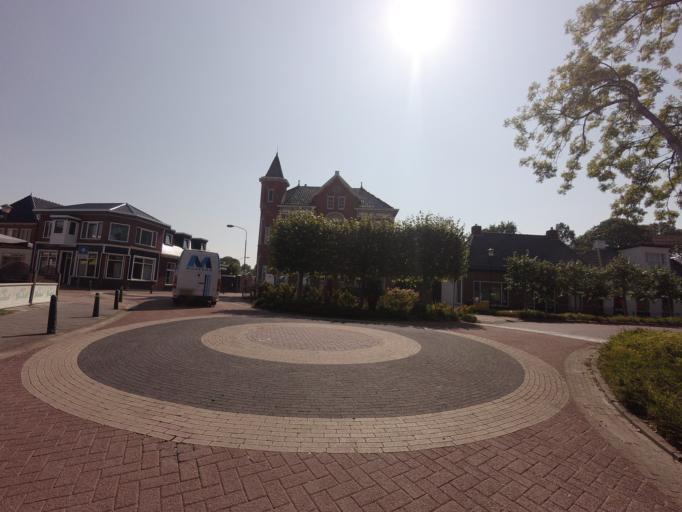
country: NL
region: Groningen
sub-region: Gemeente Zuidhorn
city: Grijpskerk
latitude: 53.2640
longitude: 6.3062
